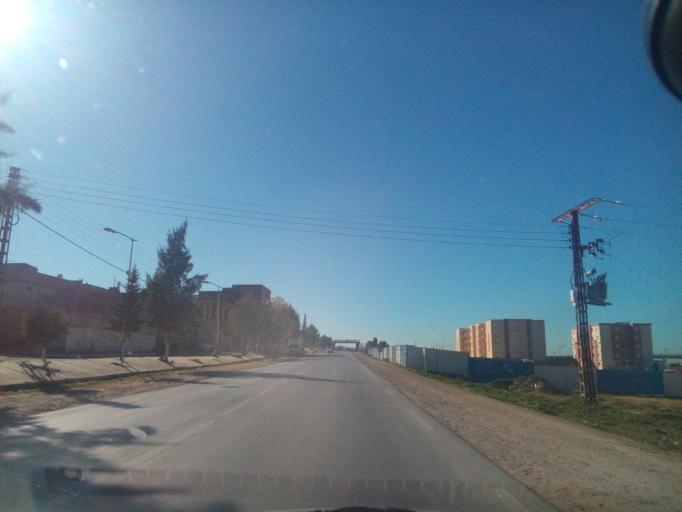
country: DZ
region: Relizane
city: Oued Rhiou
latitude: 35.9995
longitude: 1.0028
